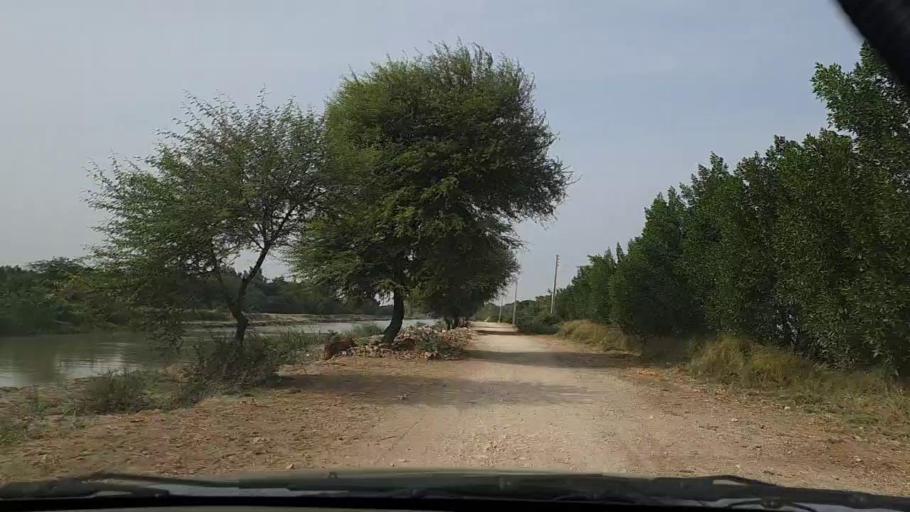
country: PK
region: Sindh
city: Thatta
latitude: 24.5696
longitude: 67.8590
